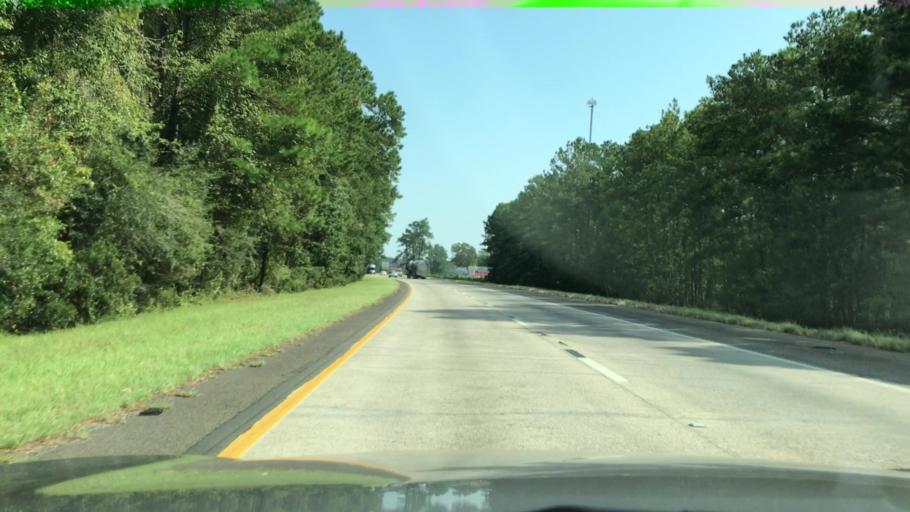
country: US
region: South Carolina
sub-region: Hampton County
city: Yemassee
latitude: 32.7908
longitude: -80.7773
